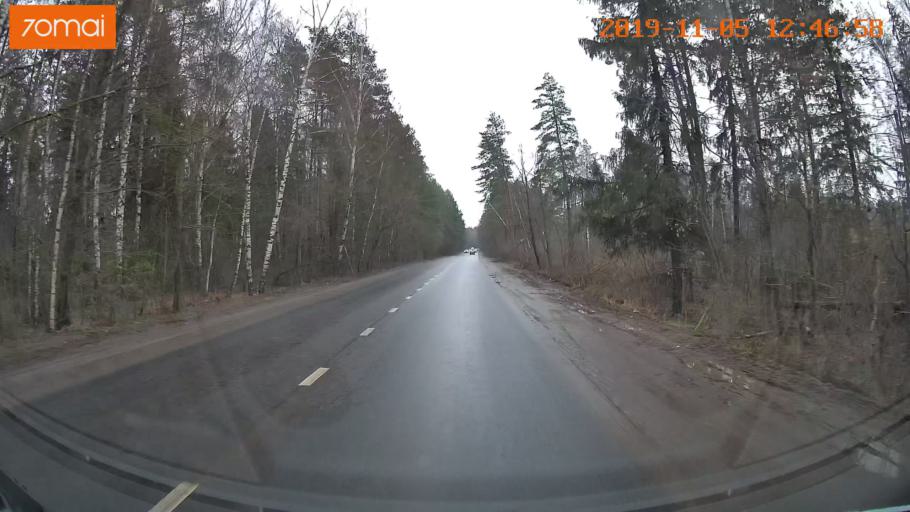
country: RU
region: Ivanovo
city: Kokhma
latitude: 56.9710
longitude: 41.0823
